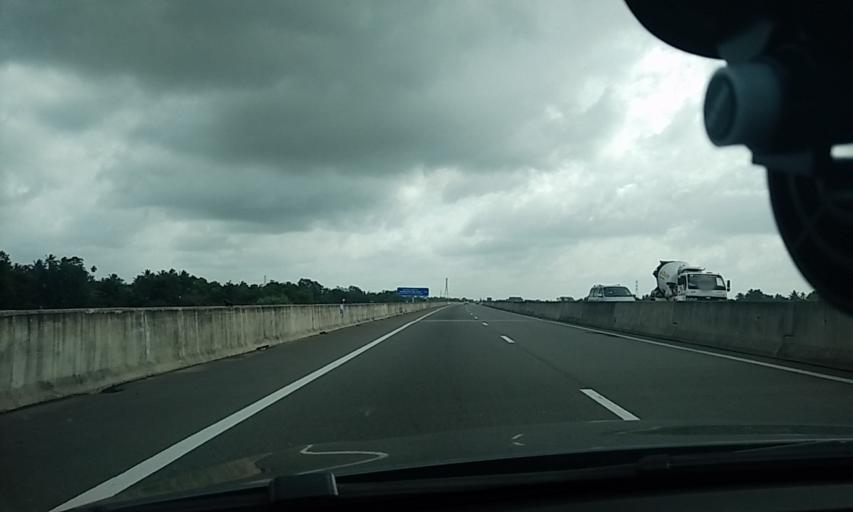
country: LK
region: Western
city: Mulleriyawa
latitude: 6.9046
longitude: 79.9799
